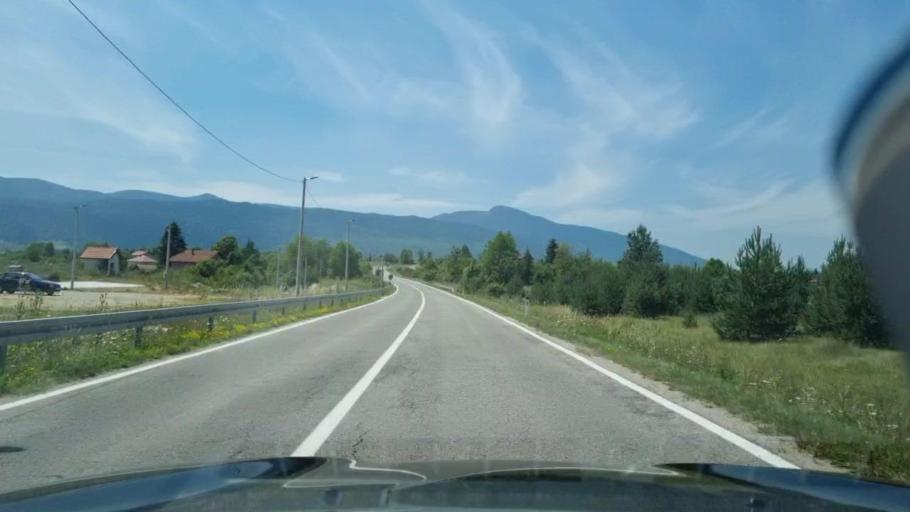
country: BA
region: Federation of Bosnia and Herzegovina
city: Sanica
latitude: 44.5378
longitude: 16.3970
